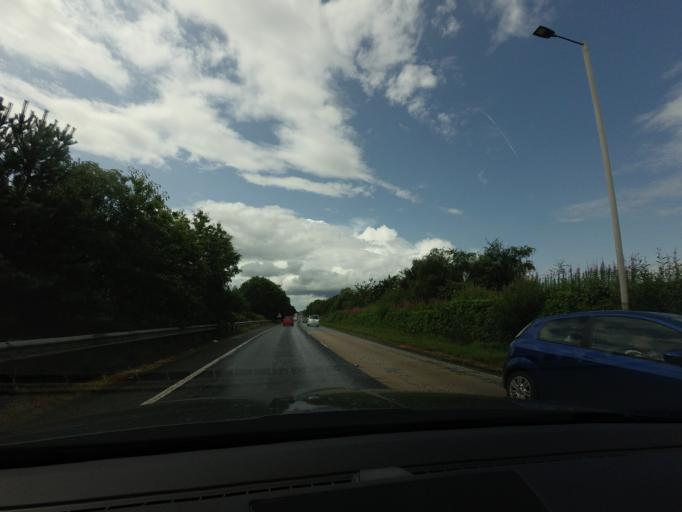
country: GB
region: Scotland
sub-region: Moray
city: Lhanbryd
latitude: 57.6330
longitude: -3.2173
